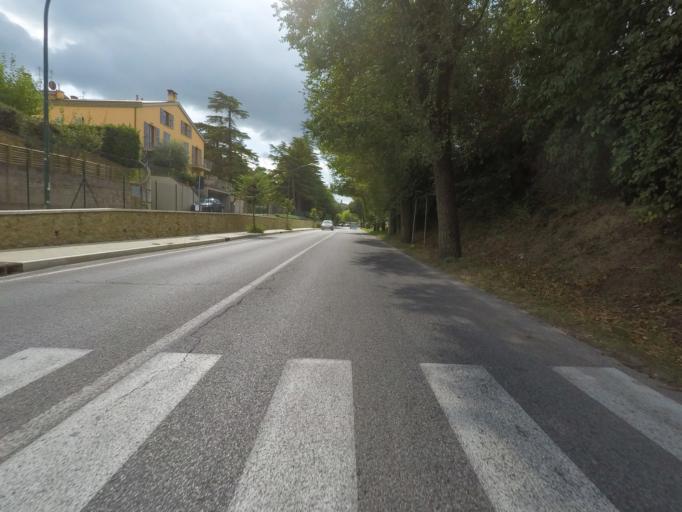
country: IT
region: Tuscany
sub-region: Provincia di Siena
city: Montepulciano
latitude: 43.1065
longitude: 11.7861
